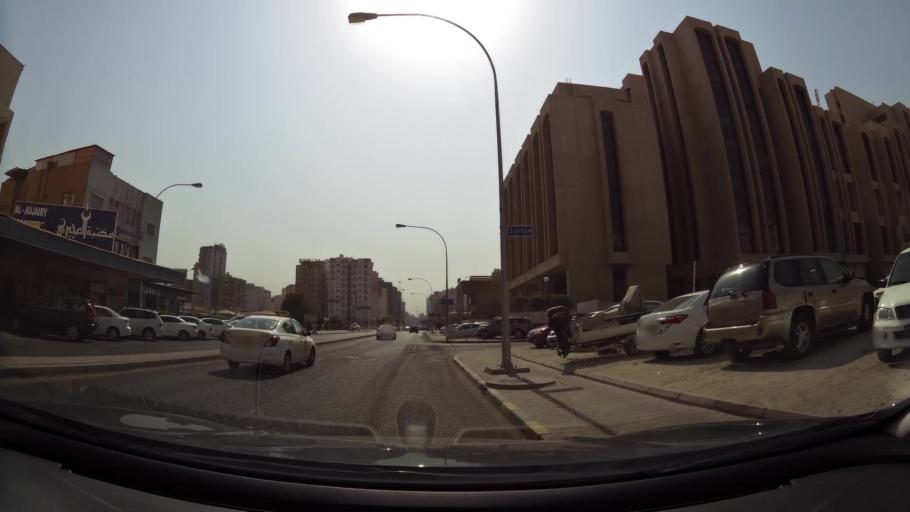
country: KW
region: Muhafazat Hawalli
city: Hawalli
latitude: 29.3337
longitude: 48.0086
